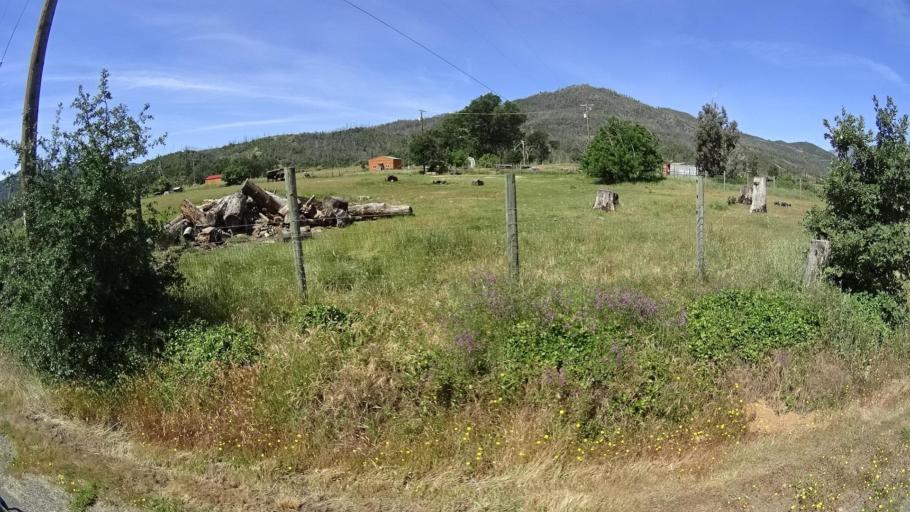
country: US
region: California
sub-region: Lake County
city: Middletown
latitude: 38.7564
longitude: -122.6402
